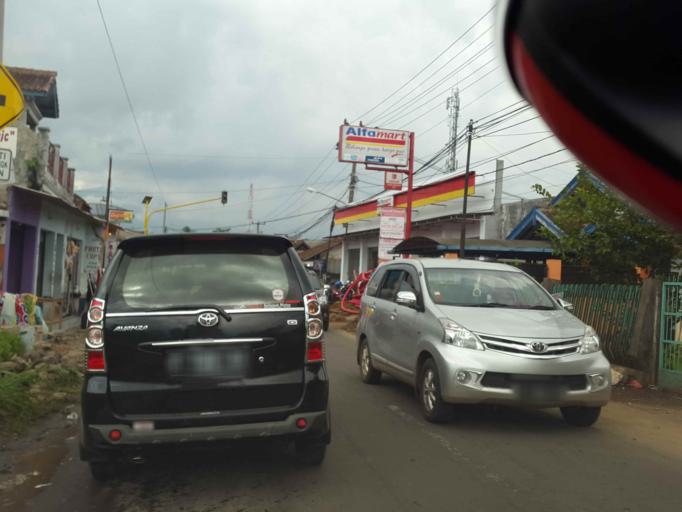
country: ID
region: West Java
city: Sukabumi
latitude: -6.9530
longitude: 106.9118
